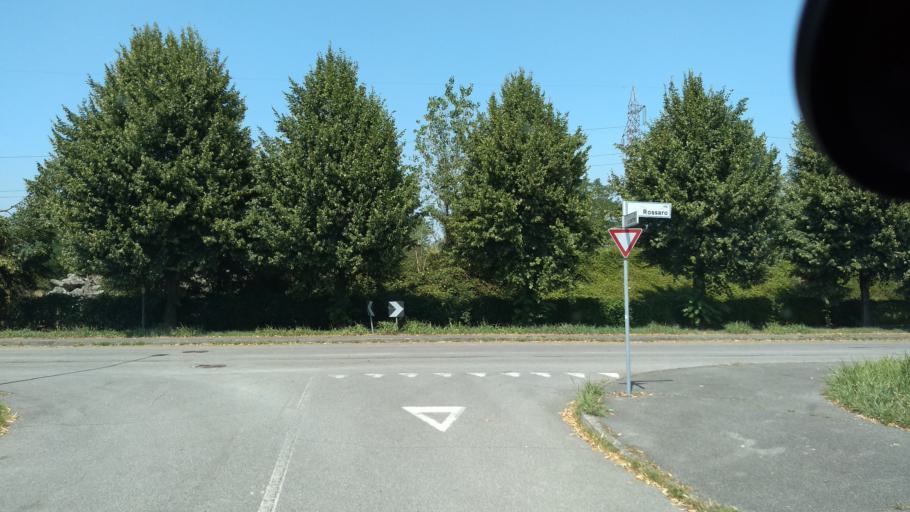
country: IT
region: Lombardy
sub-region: Provincia di Bergamo
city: Treviglio
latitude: 45.5131
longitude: 9.5746
